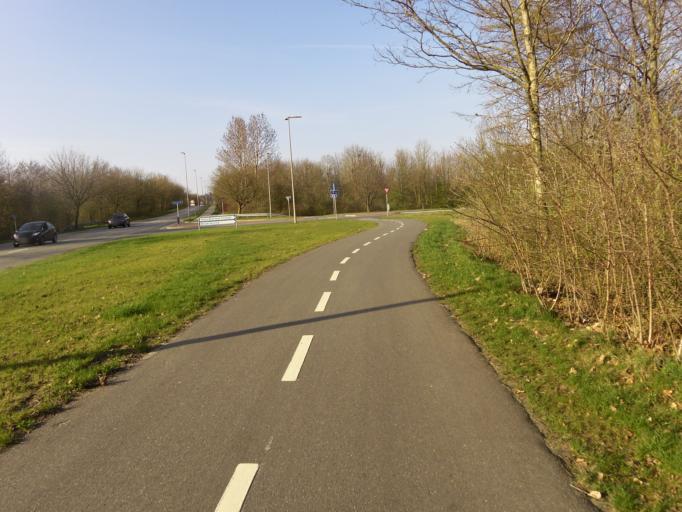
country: DK
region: South Denmark
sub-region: Vejen Kommune
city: Vejen
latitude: 55.4767
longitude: 9.1236
